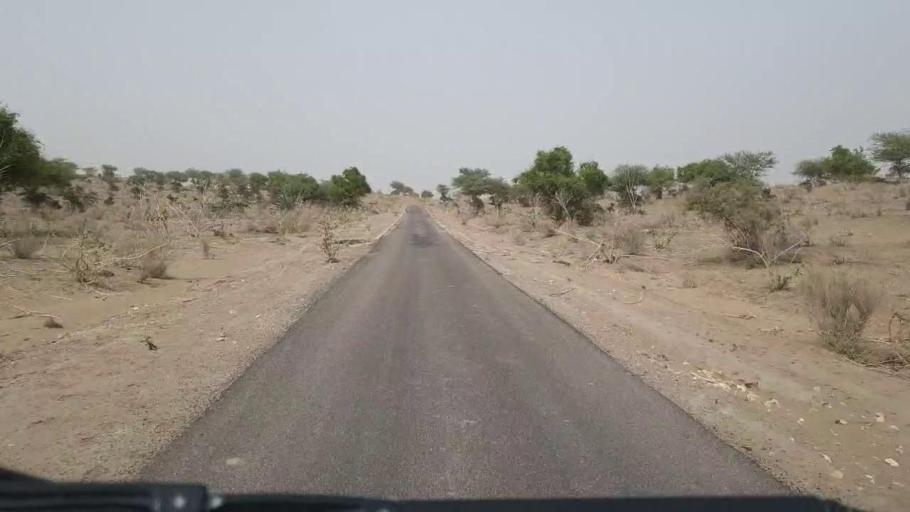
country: PK
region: Sindh
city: Islamkot
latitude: 25.3718
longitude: 70.5261
